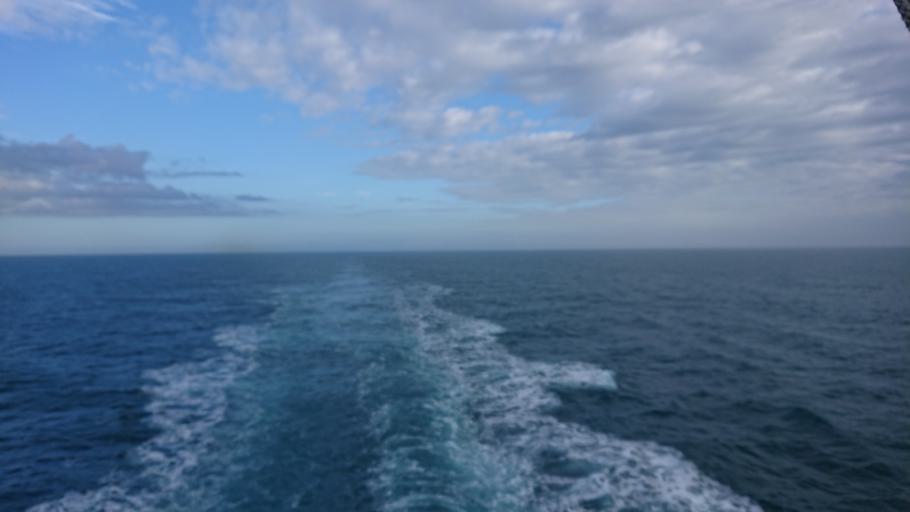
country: GB
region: Wales
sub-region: Pembrokeshire
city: Saint David's
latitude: 52.1428
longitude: -5.6607
